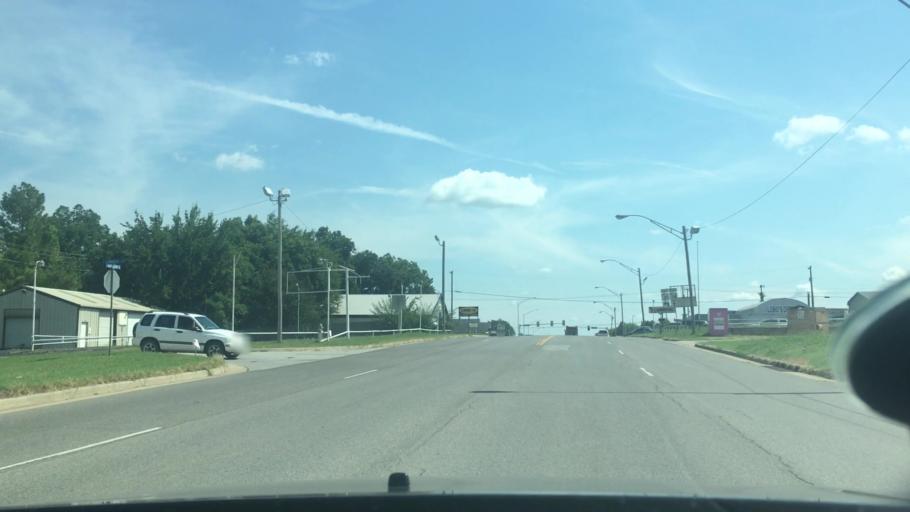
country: US
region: Oklahoma
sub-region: Pottawatomie County
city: Shawnee
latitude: 35.3349
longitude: -96.9121
